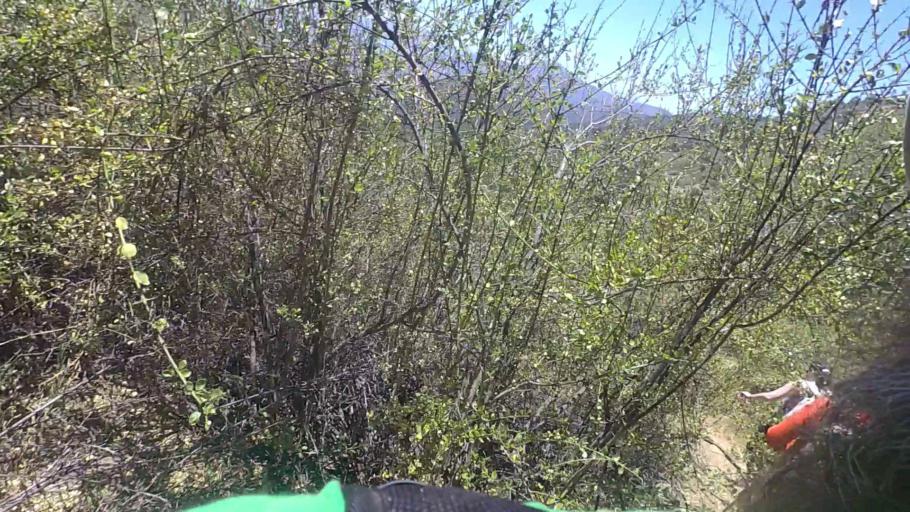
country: CL
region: Valparaiso
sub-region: Provincia de Quillota
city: Quillota
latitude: -32.9707
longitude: -71.0918
